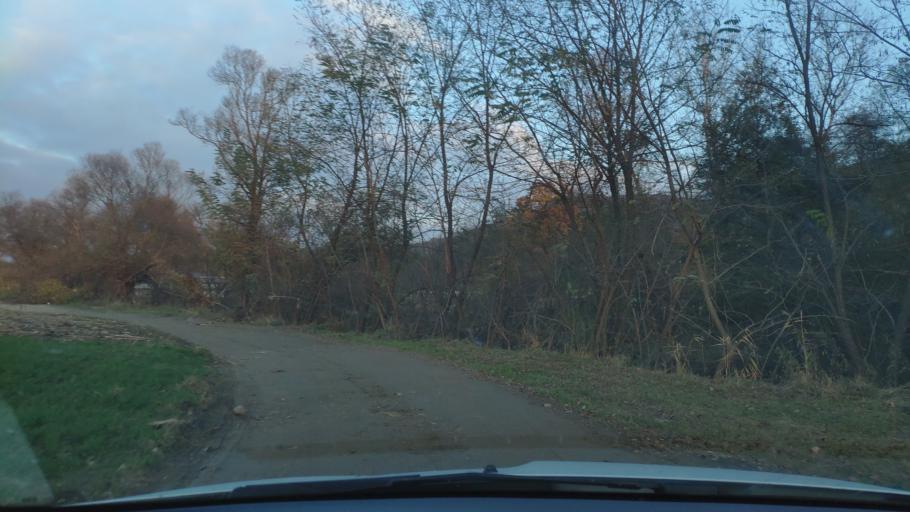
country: RO
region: Mures
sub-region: Comuna Chibed
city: Chibed
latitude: 46.5351
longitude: 24.9784
